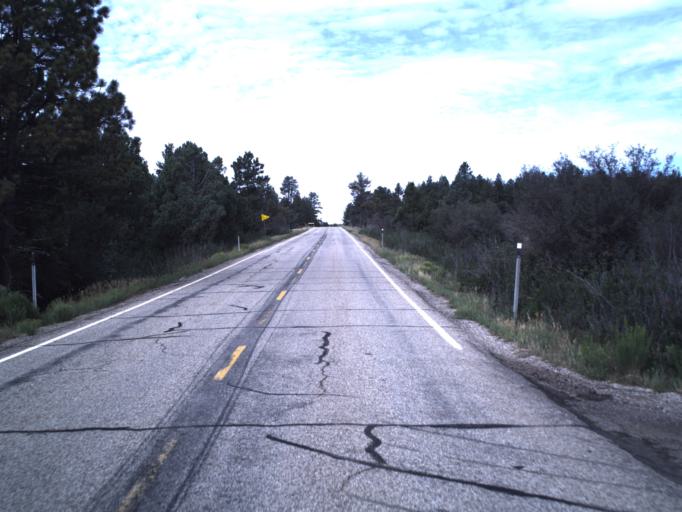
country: US
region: Utah
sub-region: Garfield County
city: Panguitch
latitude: 37.4931
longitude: -112.5594
